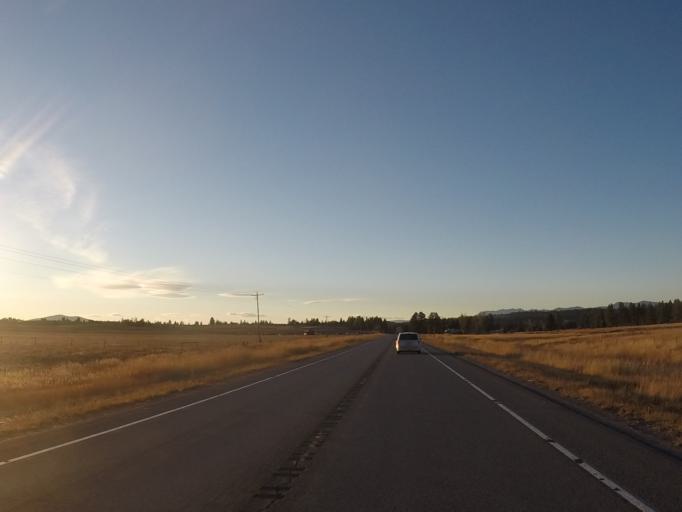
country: US
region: Montana
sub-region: Lewis and Clark County
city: Lincoln
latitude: 46.9936
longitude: -113.0211
